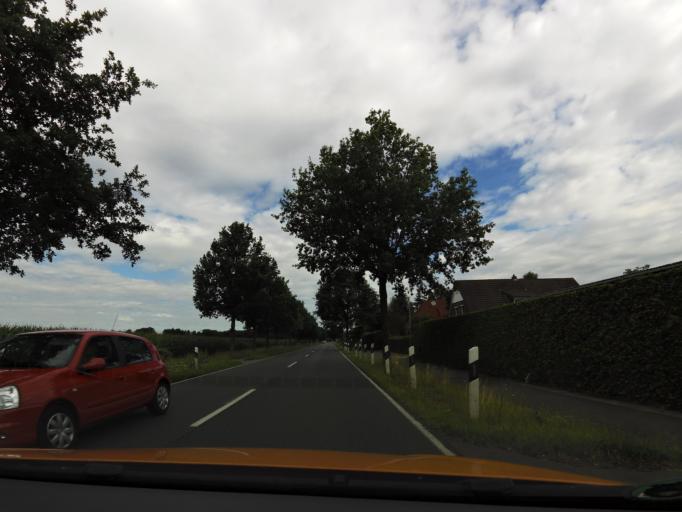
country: DE
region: Lower Saxony
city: Wiefelstede
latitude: 53.1755
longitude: 8.1304
